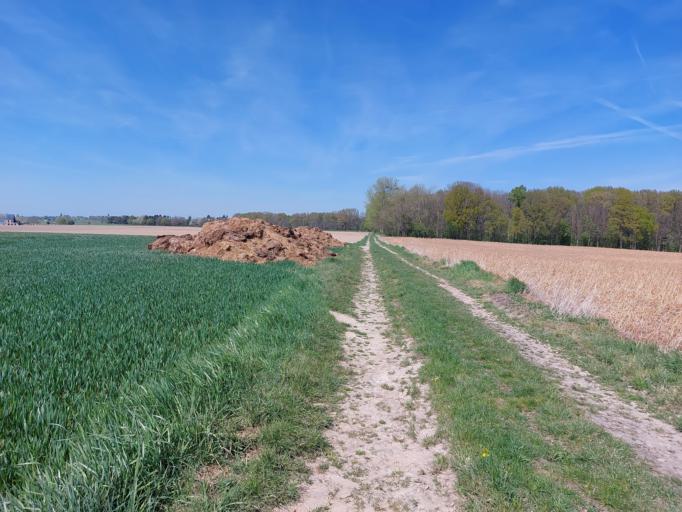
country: BE
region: Wallonia
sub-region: Province du Hainaut
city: Silly
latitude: 50.6129
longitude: 3.9702
